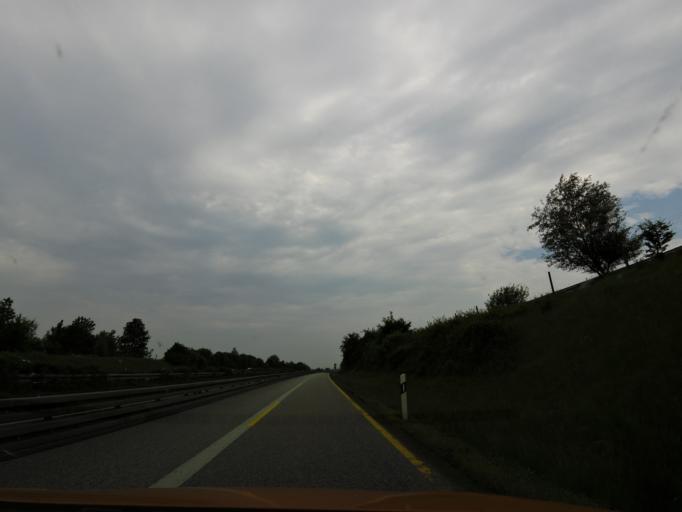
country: DE
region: Mecklenburg-Vorpommern
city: Wismar
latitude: 53.8625
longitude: 11.3981
